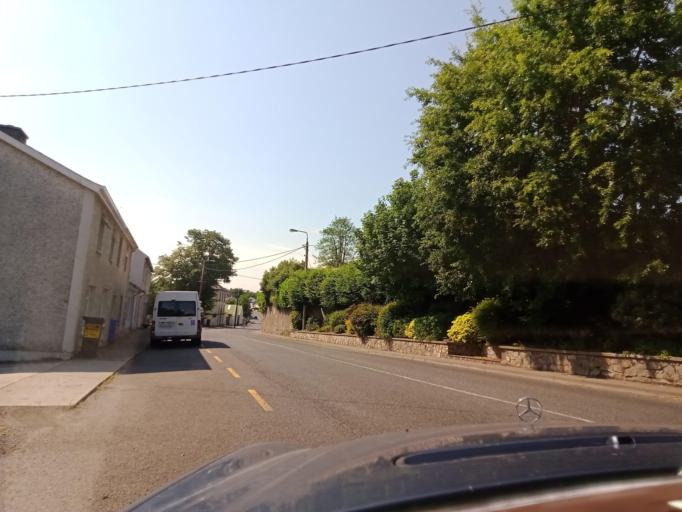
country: IE
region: Leinster
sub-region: Kilkenny
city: Piltown
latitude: 52.3496
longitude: -7.3238
